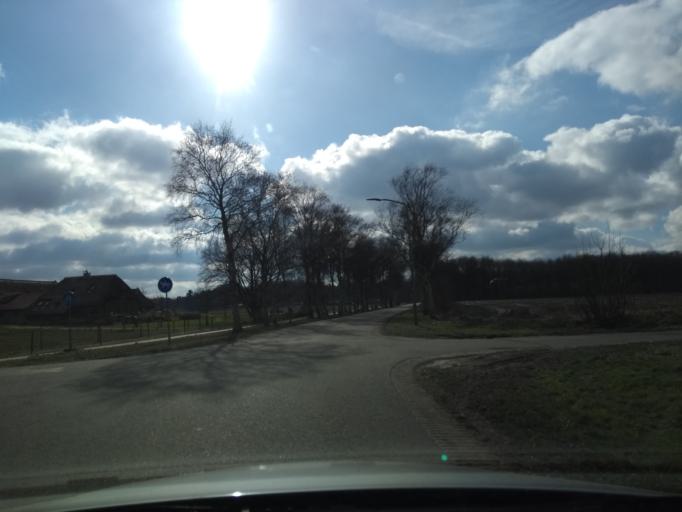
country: NL
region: Drenthe
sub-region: Gemeente Westerveld
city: Dwingeloo
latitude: 52.8253
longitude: 6.3698
